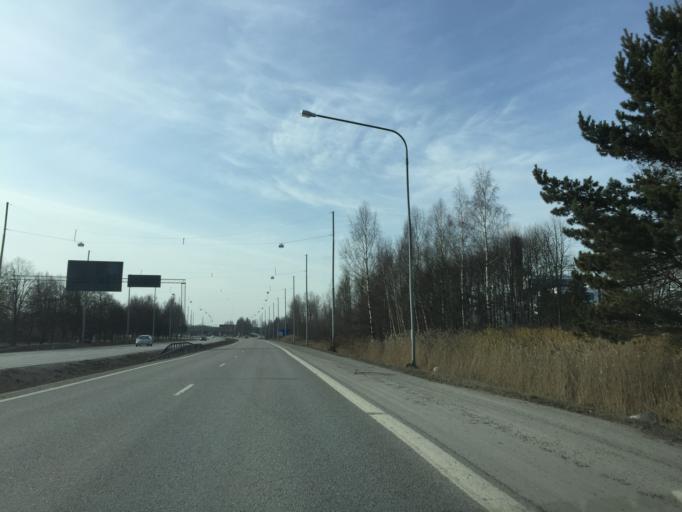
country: SE
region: OErebro
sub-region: Orebro Kommun
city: Orebro
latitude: 59.2642
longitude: 15.1863
